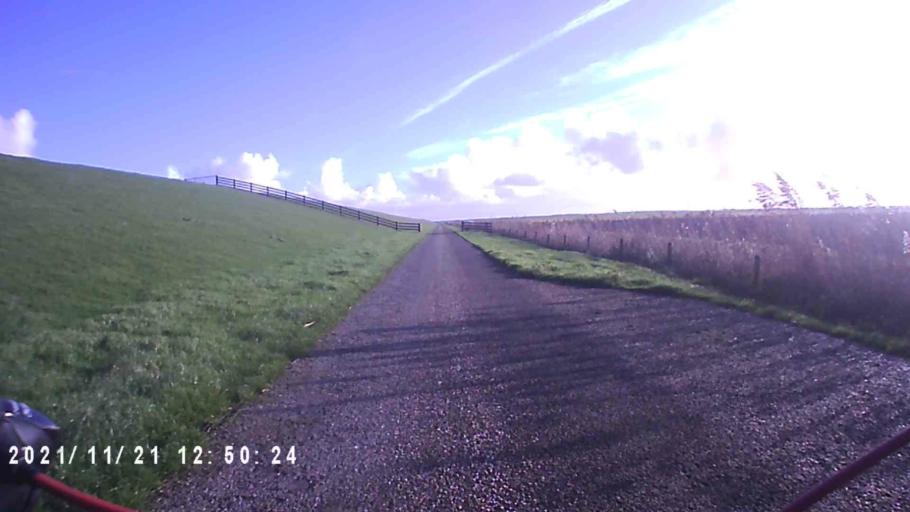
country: NL
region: Friesland
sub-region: Gemeente Dongeradeel
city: Anjum
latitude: 53.4009
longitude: 6.1194
